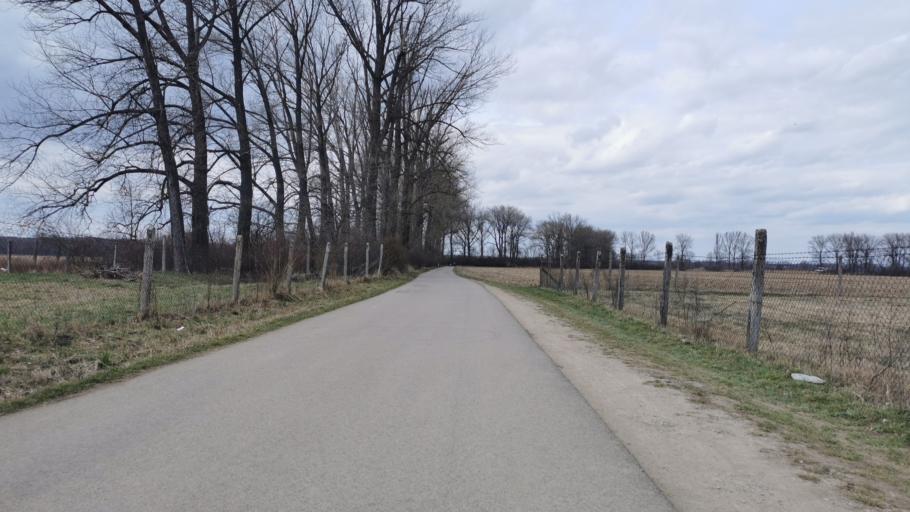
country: SK
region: Trnavsky
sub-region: Okres Skalica
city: Skalica
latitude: 48.8577
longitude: 17.2245
